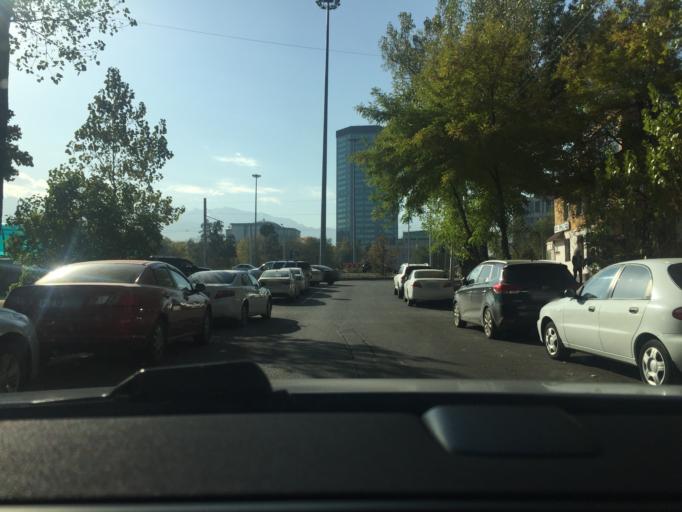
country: KZ
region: Almaty Qalasy
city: Almaty
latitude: 43.2412
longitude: 76.9146
